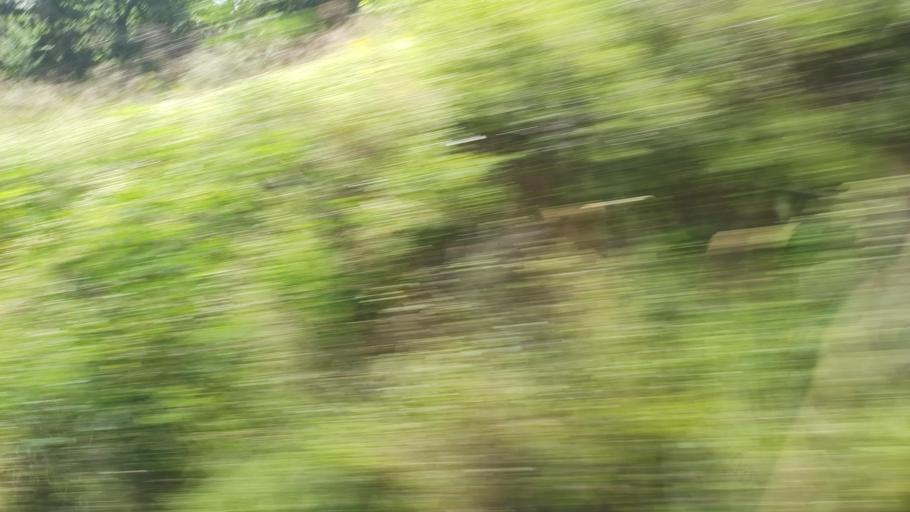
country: RO
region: Mehedinti
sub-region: Comuna Eselnita
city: Eselnita
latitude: 44.6871
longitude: 22.3625
